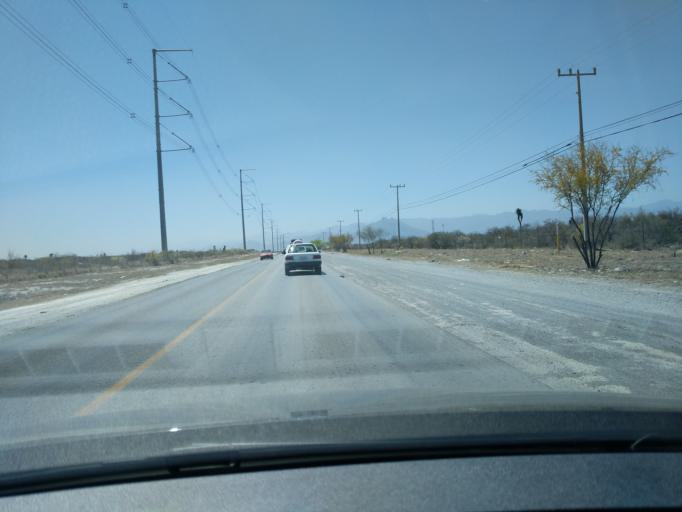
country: MX
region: Nuevo Leon
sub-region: Apodaca
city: Artemio Trevino
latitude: 25.8274
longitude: -100.1431
